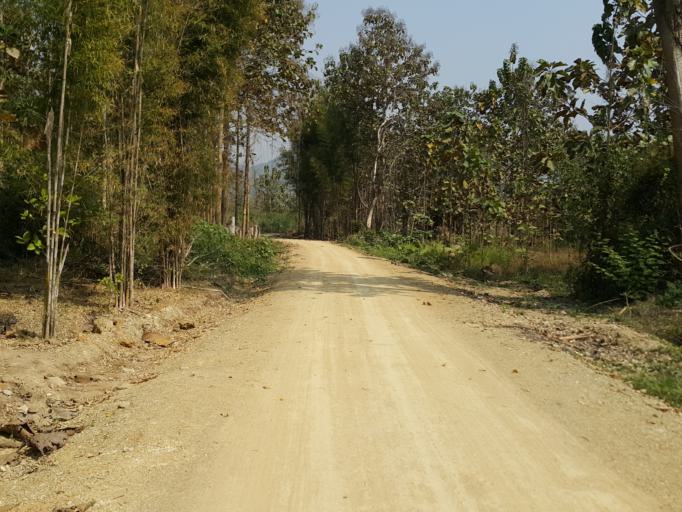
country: TH
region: Sukhothai
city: Thung Saliam
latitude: 17.3351
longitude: 99.4600
